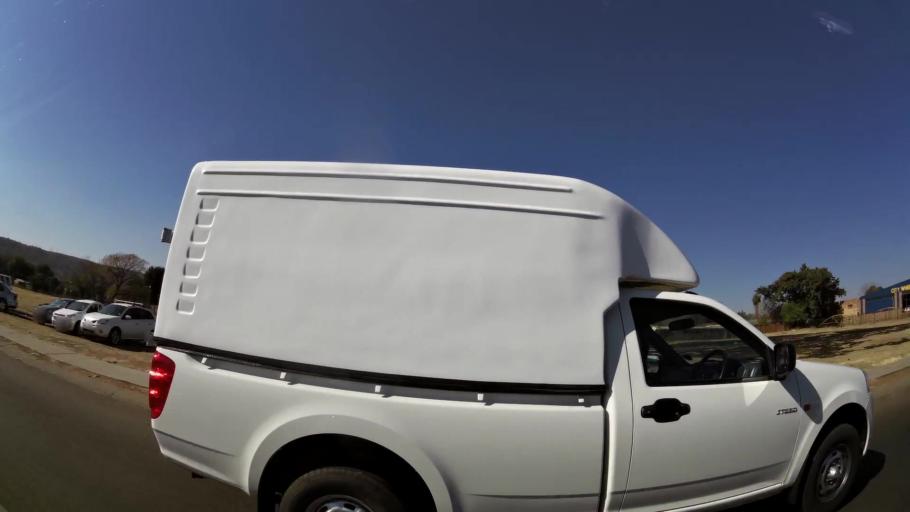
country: ZA
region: Gauteng
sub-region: City of Tshwane Metropolitan Municipality
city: Pretoria
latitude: -25.7115
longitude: 28.2030
